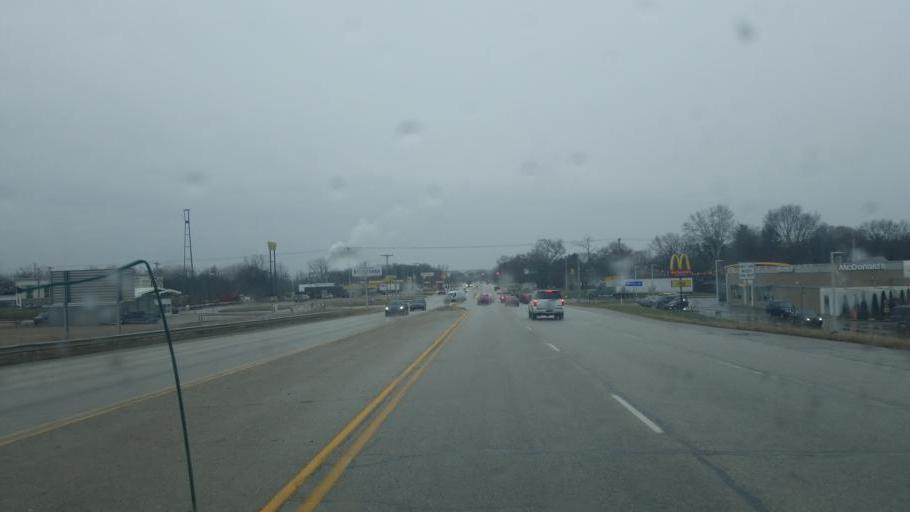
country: US
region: Indiana
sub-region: Shelby County
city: Shelbyville
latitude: 39.5489
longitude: -85.7757
